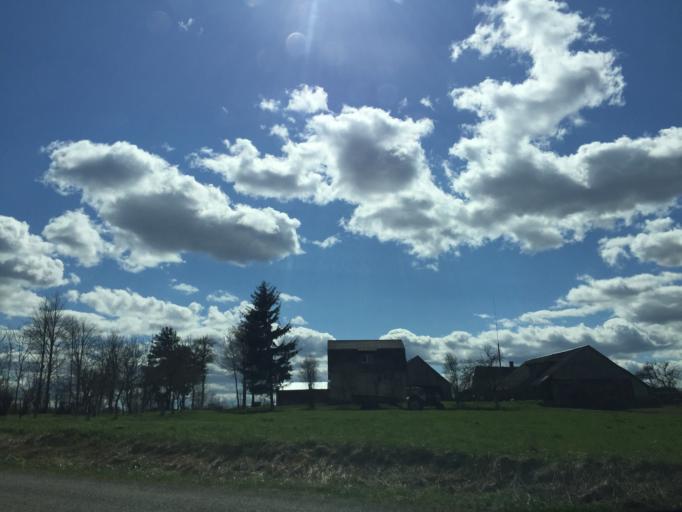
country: LV
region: Rezekne
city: Rezekne
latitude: 56.5764
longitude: 27.1319
